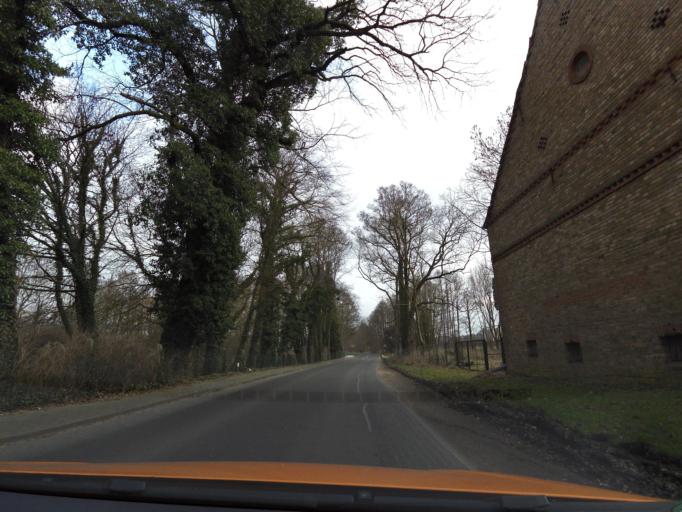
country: DE
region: Brandenburg
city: Walsleben
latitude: 52.9379
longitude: 12.6664
